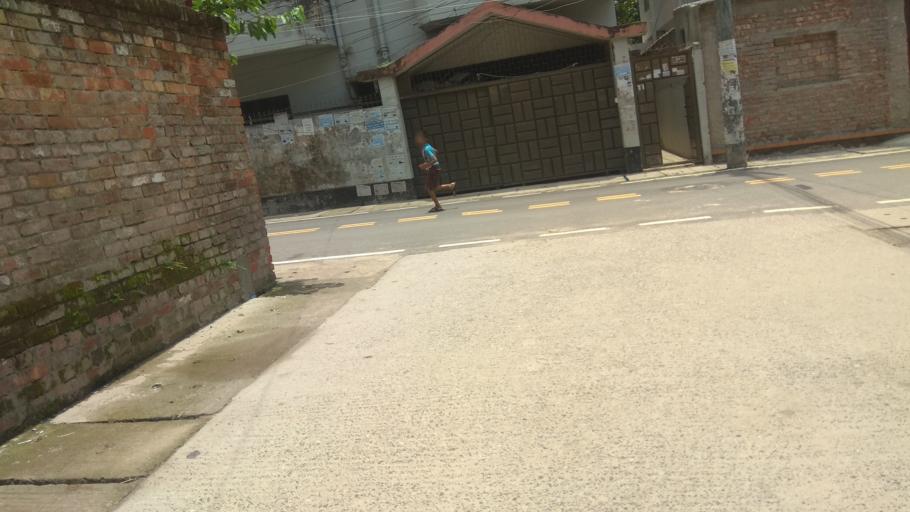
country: BD
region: Dhaka
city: Tungi
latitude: 23.8187
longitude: 90.3579
